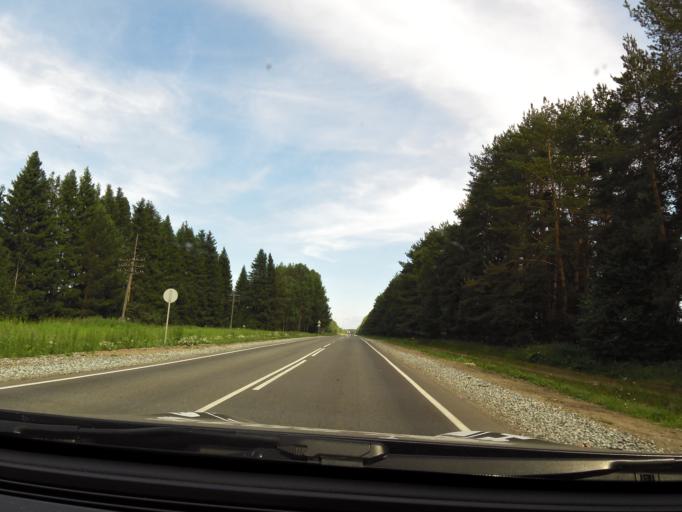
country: RU
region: Kirov
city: Slobodskoy
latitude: 58.7798
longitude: 50.4477
